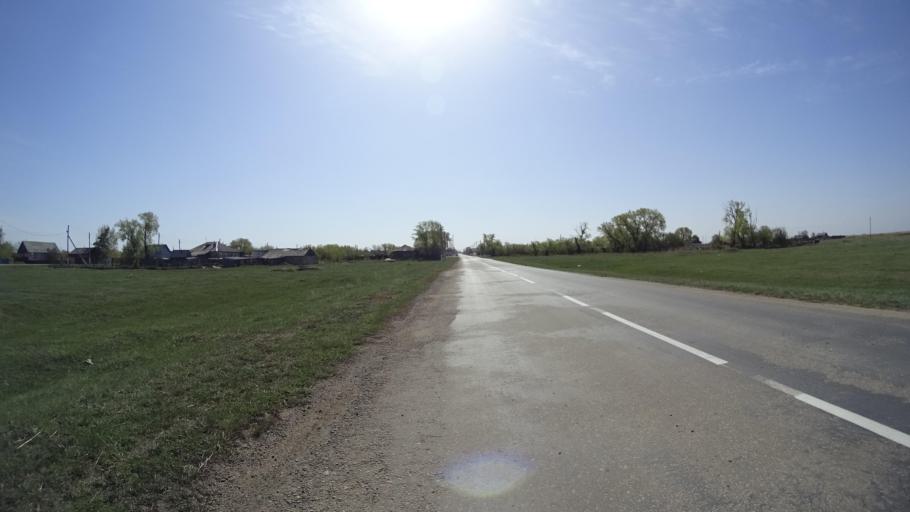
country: RU
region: Chelyabinsk
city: Chesma
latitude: 53.8021
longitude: 61.0158
